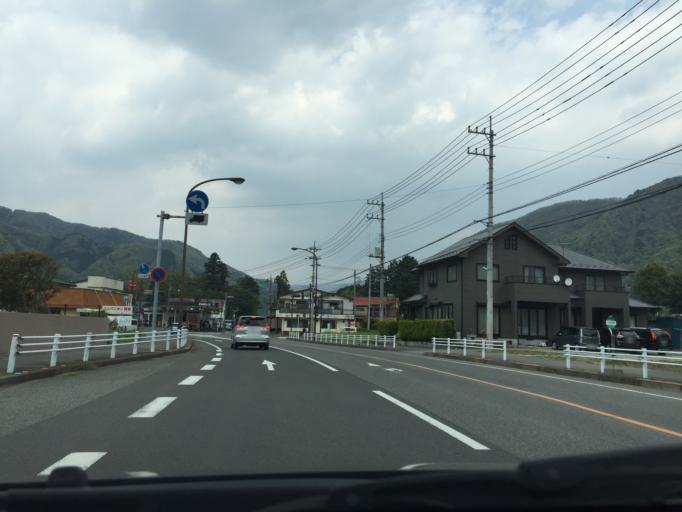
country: JP
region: Tochigi
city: Imaichi
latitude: 36.8180
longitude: 139.7159
